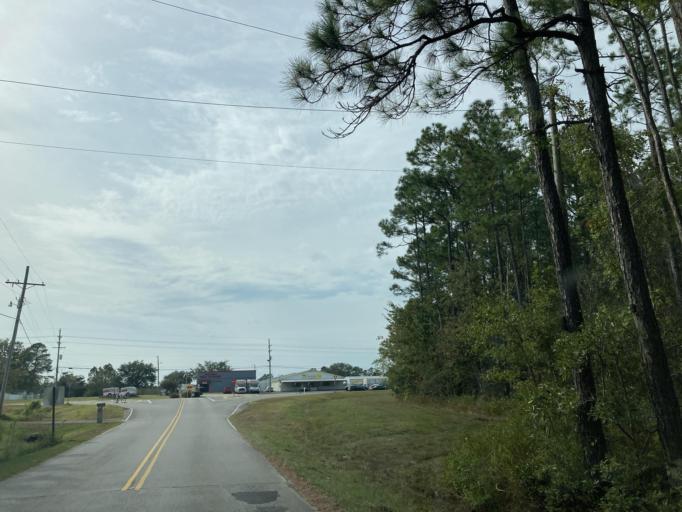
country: US
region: Mississippi
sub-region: Jackson County
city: Saint Martin
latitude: 30.4760
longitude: -88.8484
